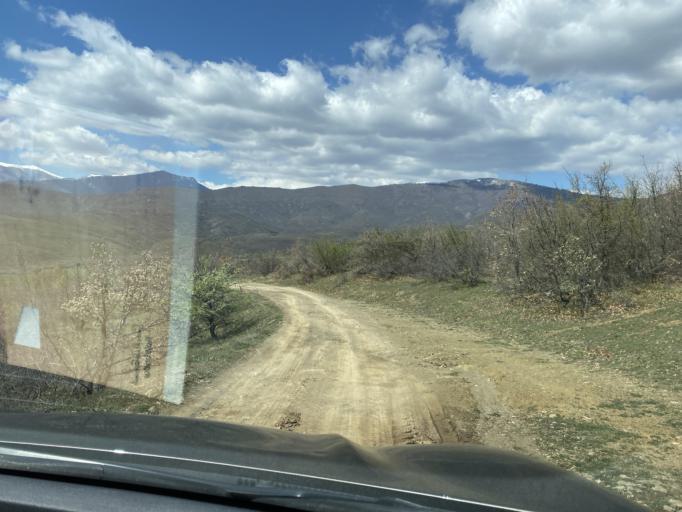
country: MK
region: Caska
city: Caska
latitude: 41.7312
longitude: 21.6561
